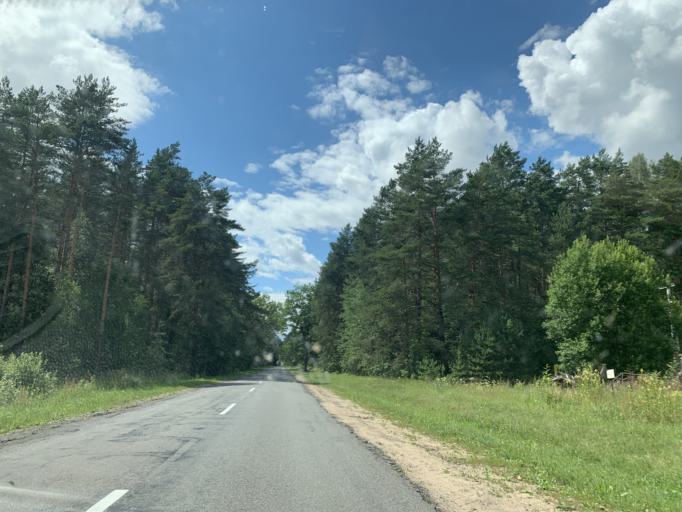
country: BY
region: Minsk
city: Rakaw
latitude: 53.9855
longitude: 26.9770
